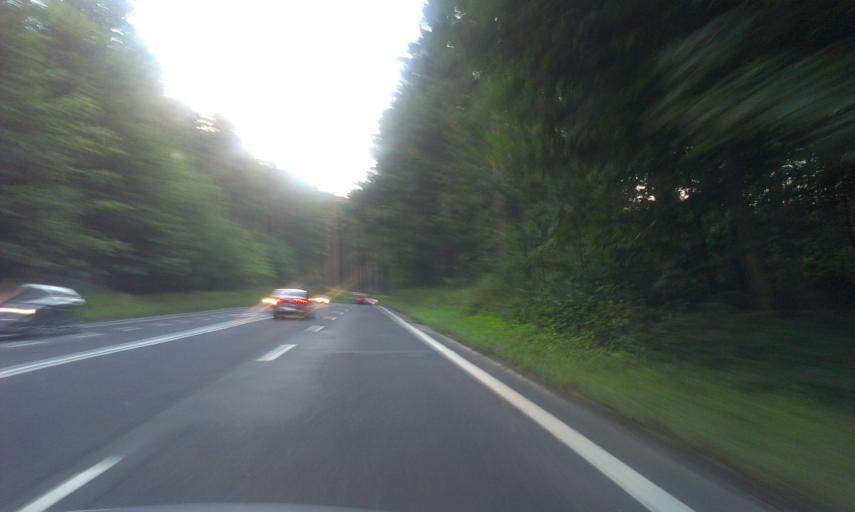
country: PL
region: West Pomeranian Voivodeship
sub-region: Koszalin
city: Koszalin
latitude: 54.2146
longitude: 16.2220
